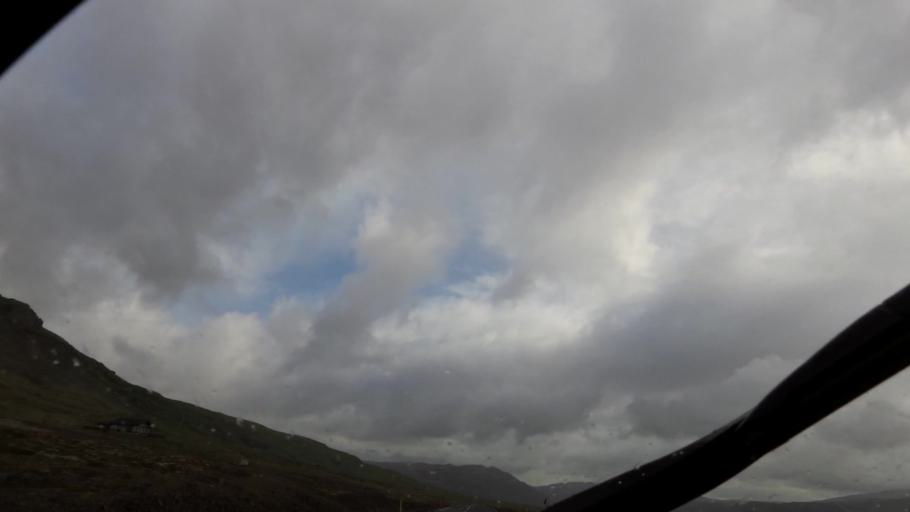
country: IS
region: Westfjords
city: Isafjoerdur
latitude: 65.5503
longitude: -23.1994
